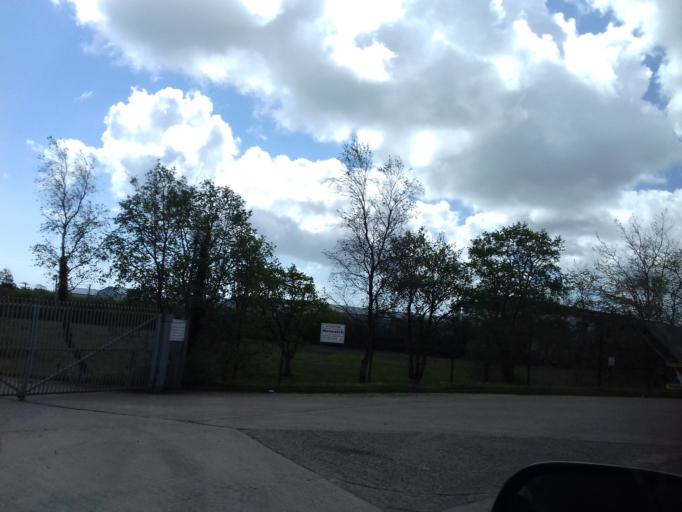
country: IE
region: Leinster
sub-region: Loch Garman
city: Castlebridge
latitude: 52.3610
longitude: -6.4521
